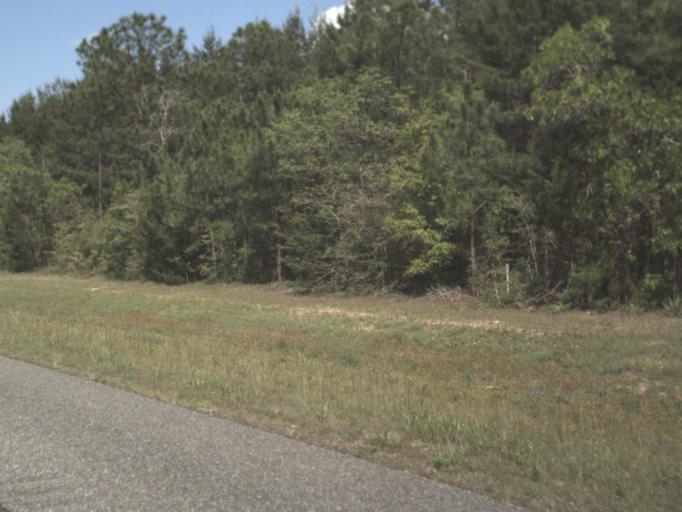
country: US
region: Florida
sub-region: Santa Rosa County
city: East Milton
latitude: 30.6768
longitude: -86.8240
